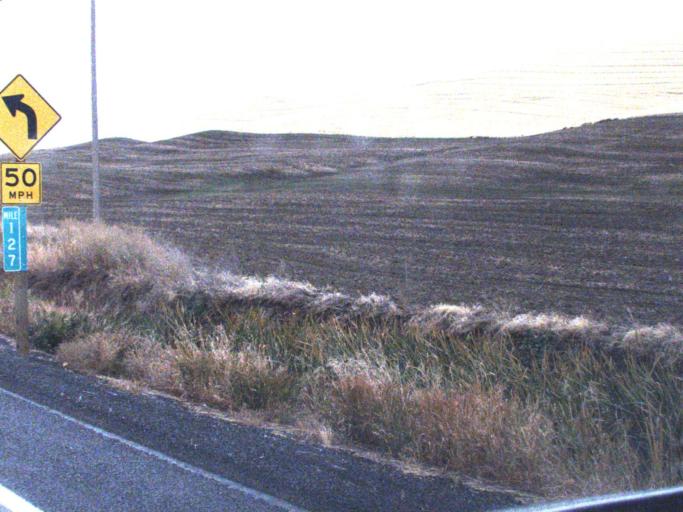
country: US
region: Washington
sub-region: Whitman County
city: Colfax
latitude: 46.8479
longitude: -117.4766
